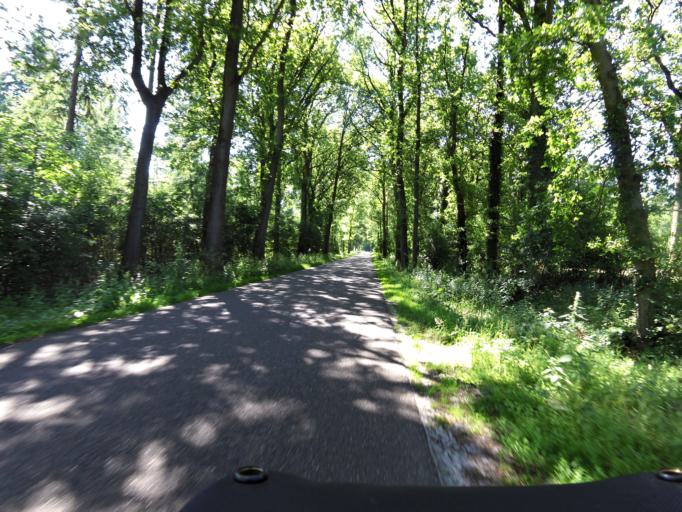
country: NL
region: Overijssel
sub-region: Gemeente Twenterand
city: Den Ham
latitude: 52.5106
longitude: 6.4939
